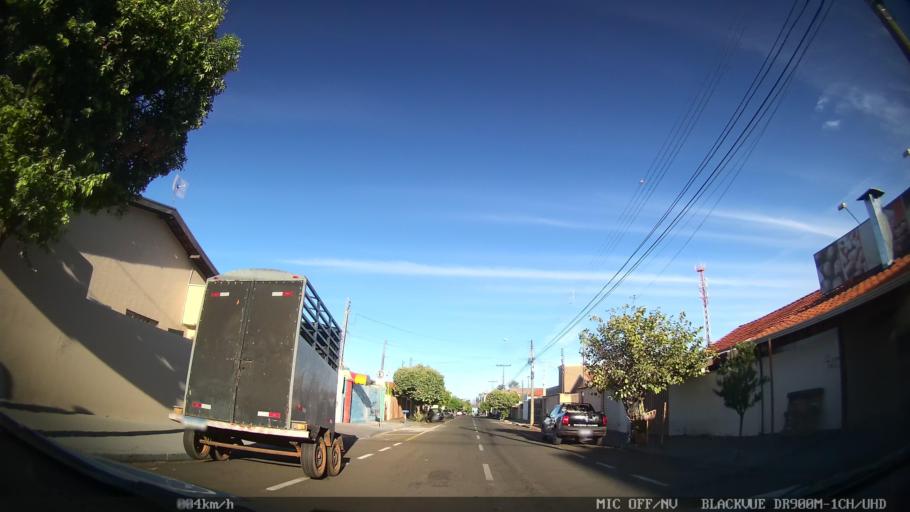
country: BR
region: Sao Paulo
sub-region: Sao Jose Do Rio Preto
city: Sao Jose do Rio Preto
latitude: -20.8308
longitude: -49.3740
